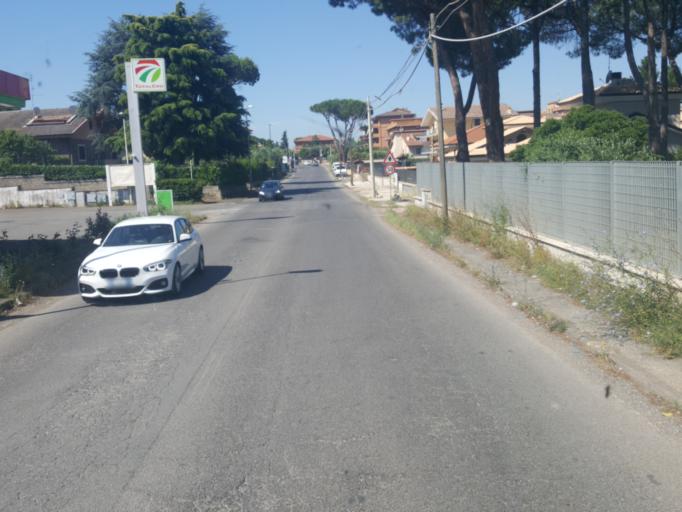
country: IT
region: Latium
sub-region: Citta metropolitana di Roma Capitale
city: Frascati
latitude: 41.8263
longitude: 12.6470
